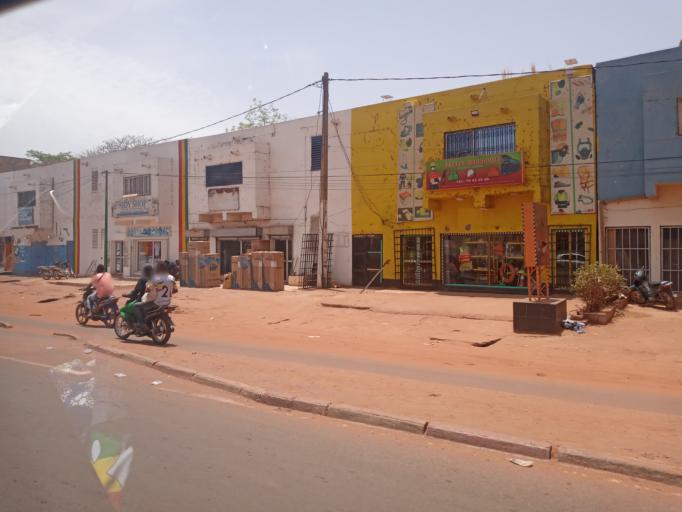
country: ML
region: Bamako
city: Bamako
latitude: 12.6152
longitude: -7.9784
